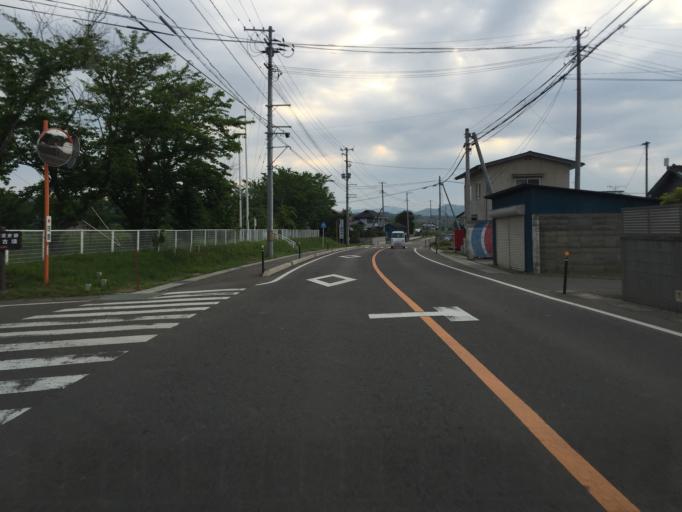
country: JP
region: Fukushima
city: Yanagawamachi-saiwaicho
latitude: 37.8767
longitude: 140.5826
